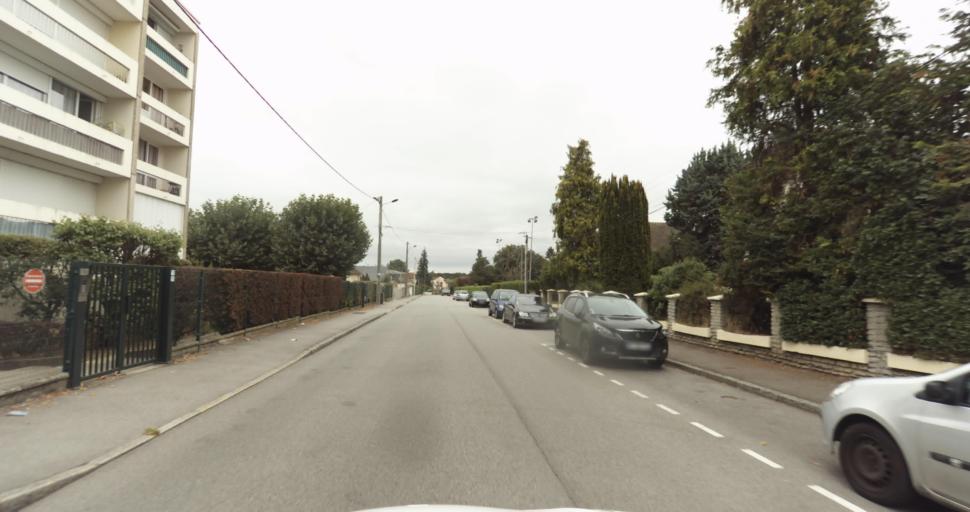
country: FR
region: Haute-Normandie
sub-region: Departement de l'Eure
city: Evreux
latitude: 49.0189
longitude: 1.1683
